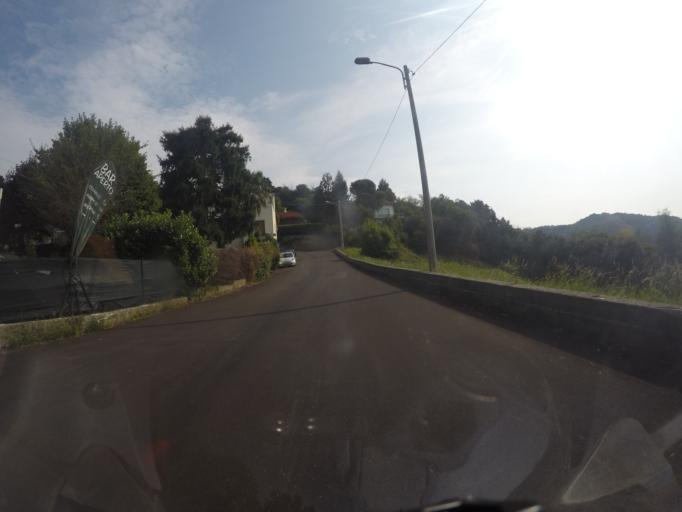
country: IT
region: Lombardy
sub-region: Provincia di Lecco
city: Santa Maria Hoe
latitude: 45.7507
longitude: 9.3882
